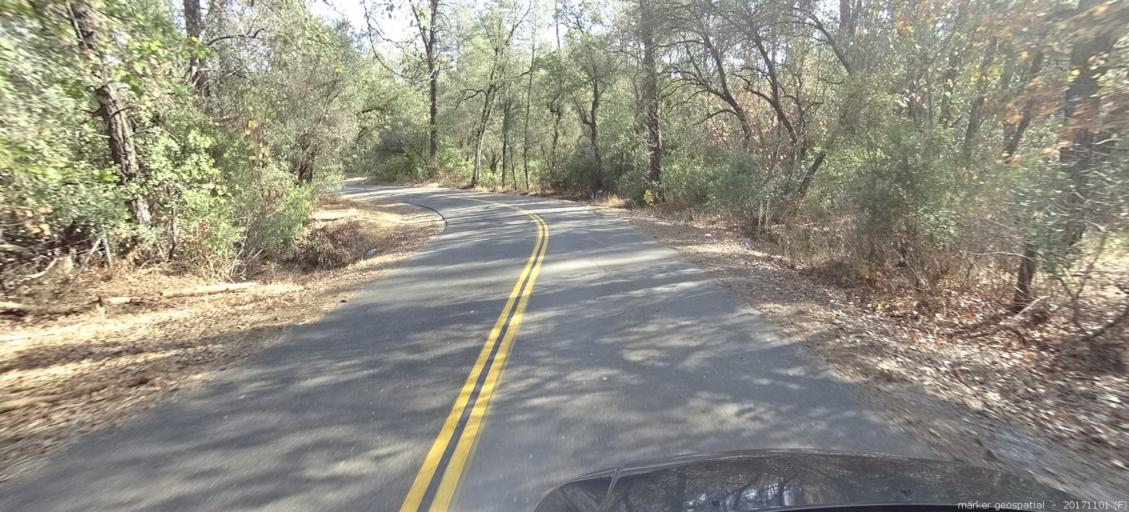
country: US
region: California
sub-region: Shasta County
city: Central Valley (historical)
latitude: 40.6782
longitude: -122.4167
